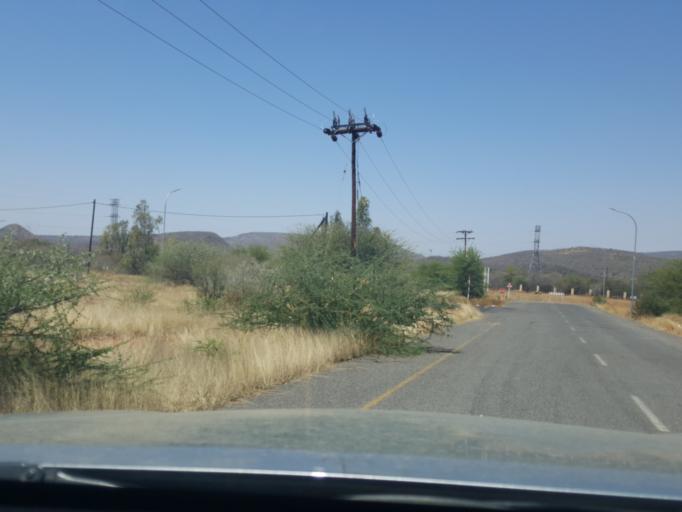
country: BW
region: South East
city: Lobatse
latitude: -25.1797
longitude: 25.6819
